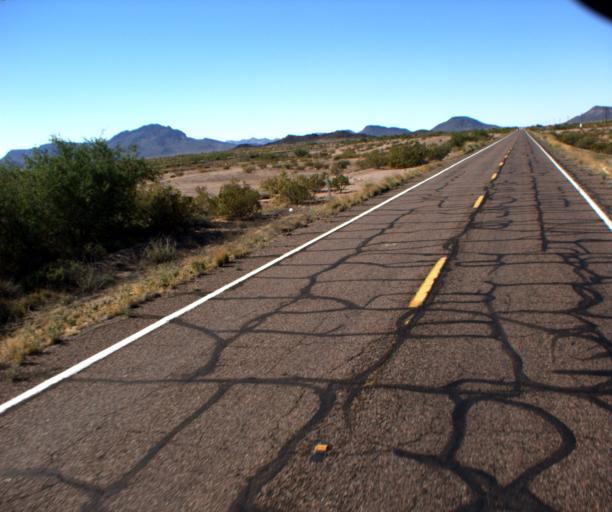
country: US
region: Arizona
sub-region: Maricopa County
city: Gila Bend
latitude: 32.8211
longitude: -112.7879
